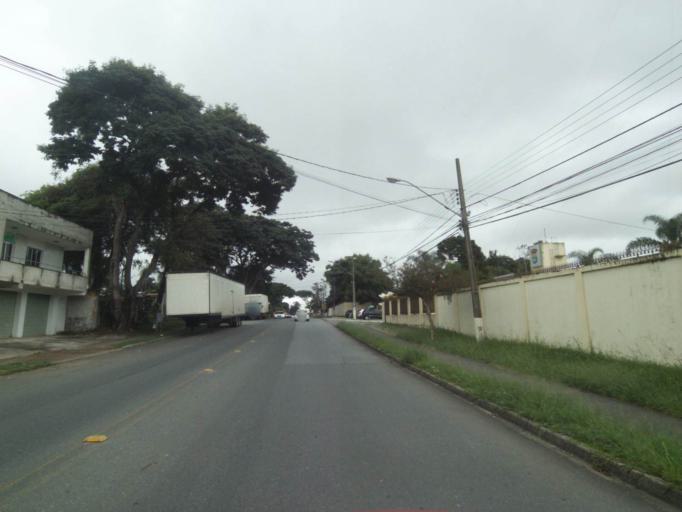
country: BR
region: Parana
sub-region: Curitiba
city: Curitiba
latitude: -25.4846
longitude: -49.2997
